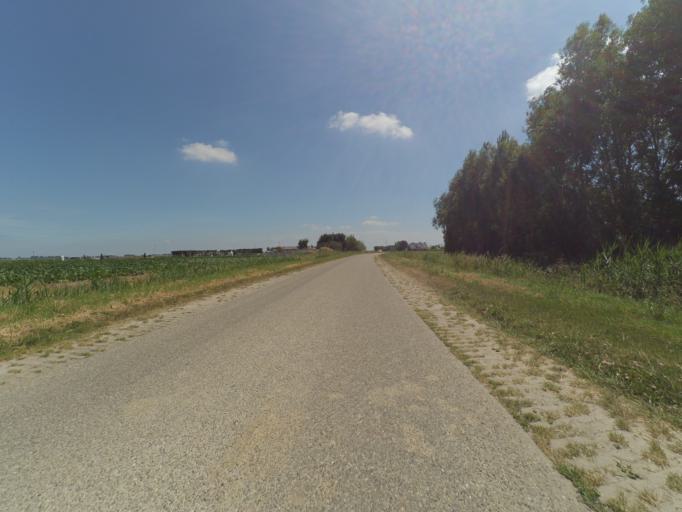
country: NL
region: Zeeland
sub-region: Gemeente Reimerswaal
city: Yerseke
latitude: 51.5771
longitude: 4.0111
